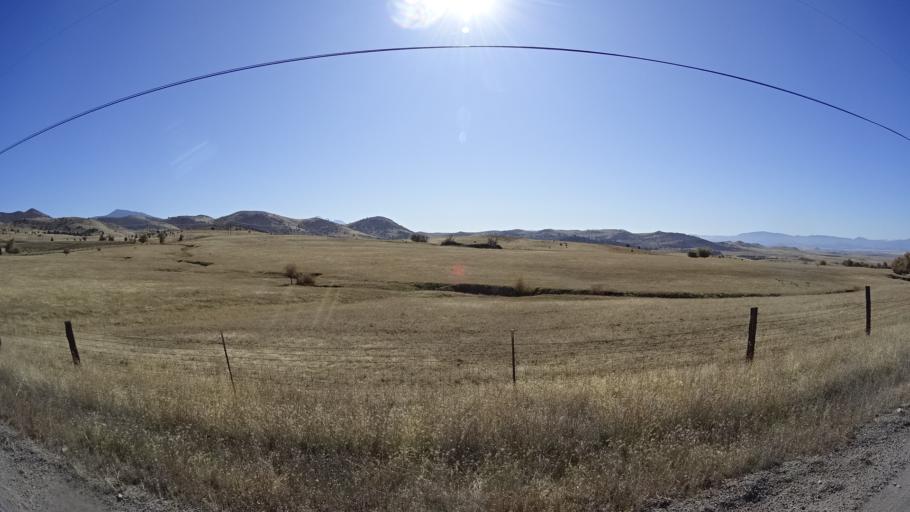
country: US
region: California
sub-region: Siskiyou County
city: Montague
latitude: 41.8299
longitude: -122.3650
